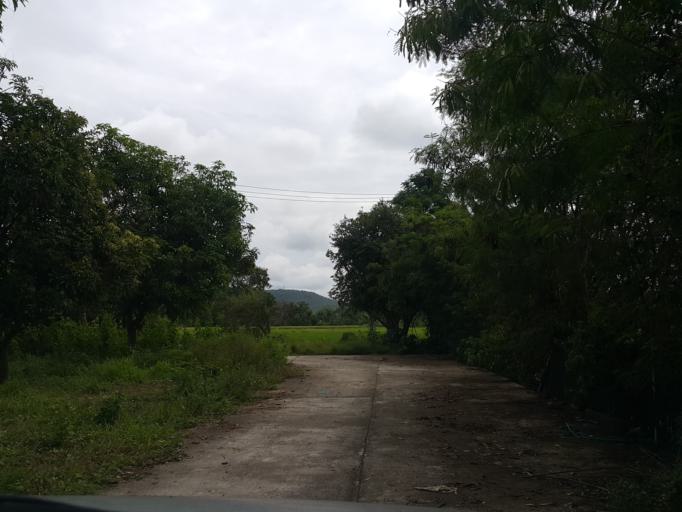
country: TH
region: Chiang Mai
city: San Sai
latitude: 18.8440
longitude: 99.1426
